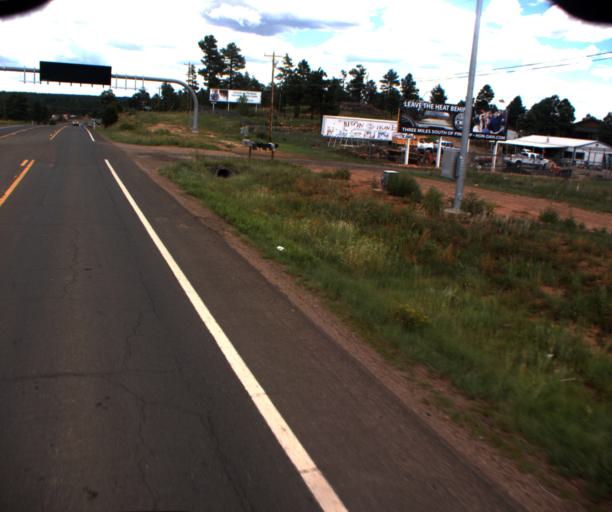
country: US
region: Arizona
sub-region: Navajo County
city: Linden
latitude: 34.2854
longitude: -110.1180
